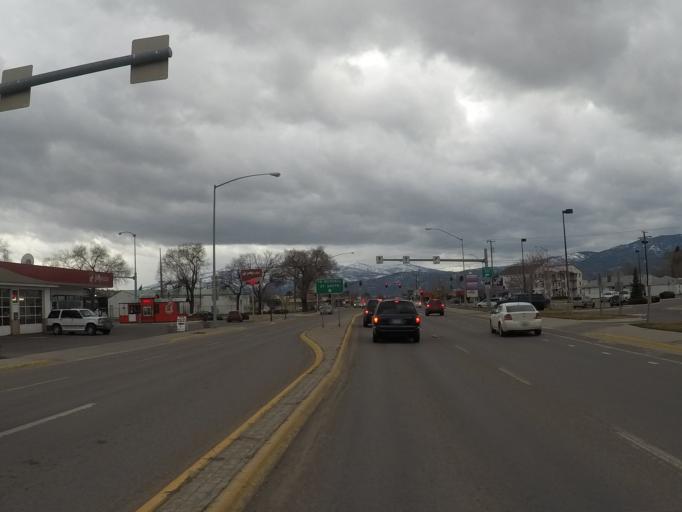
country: US
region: Montana
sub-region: Missoula County
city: Missoula
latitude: 46.8496
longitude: -114.0170
